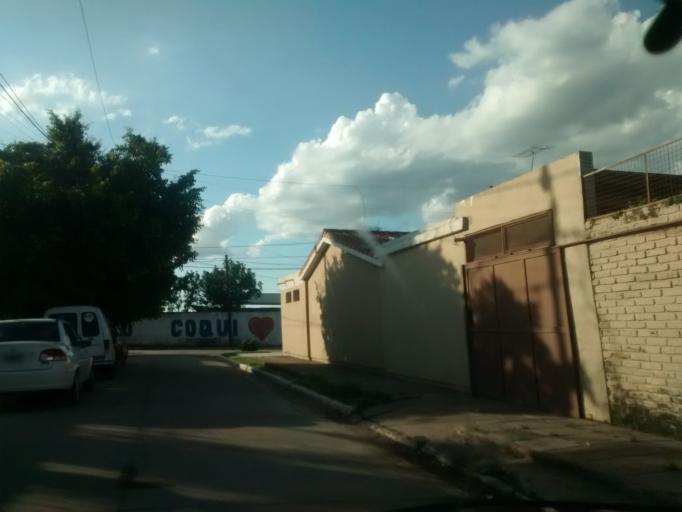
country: AR
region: Chaco
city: Fontana
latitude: -27.4404
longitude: -59.0142
